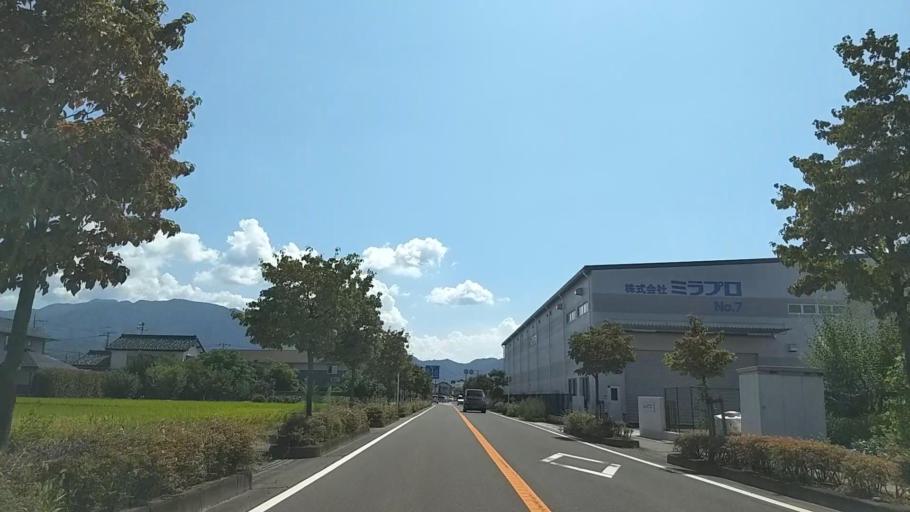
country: JP
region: Yamanashi
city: Ryuo
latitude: 35.5964
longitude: 138.5037
